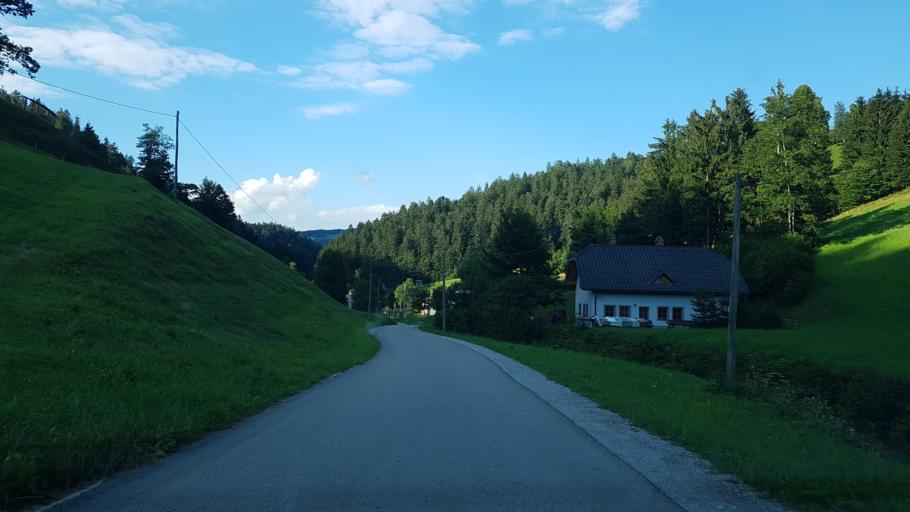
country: SI
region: Idrija
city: Spodnja Idrija
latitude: 46.0749
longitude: 14.0272
